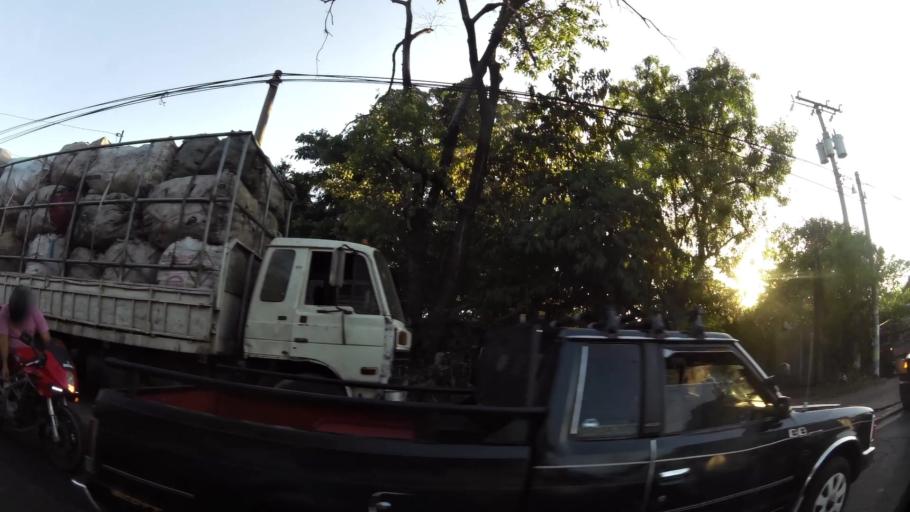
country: SV
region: La Libertad
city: Santa Tecla
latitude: 13.7212
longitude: -89.3644
